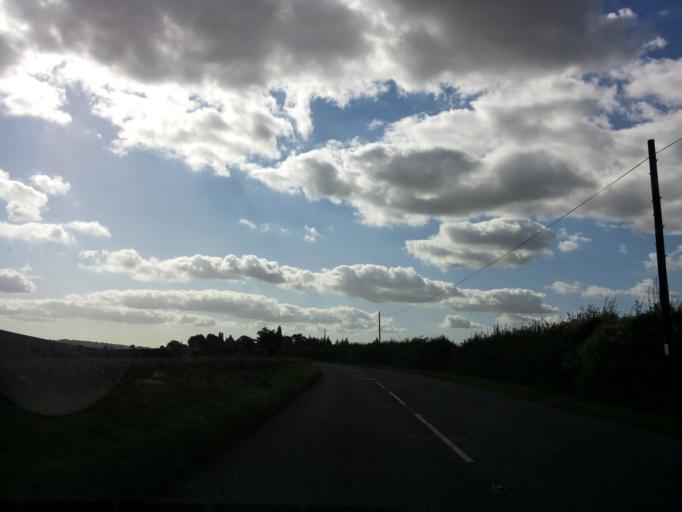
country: GB
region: England
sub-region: Bath and North East Somerset
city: Saltford
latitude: 51.3792
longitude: -2.4689
